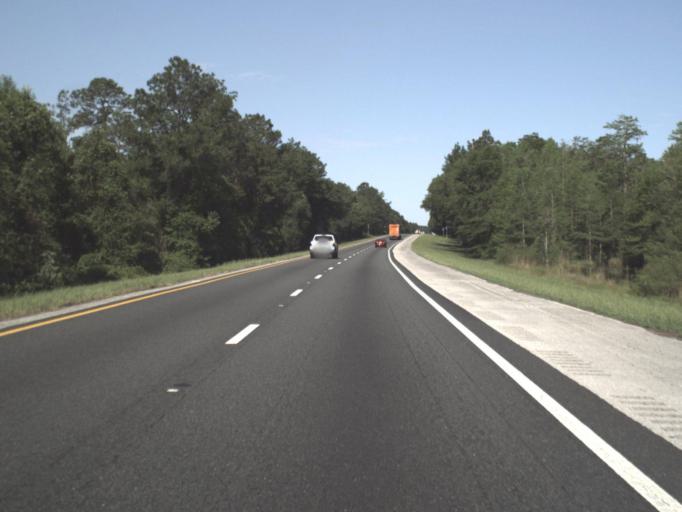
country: US
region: Florida
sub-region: Holmes County
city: Bonifay
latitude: 30.7607
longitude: -85.7323
